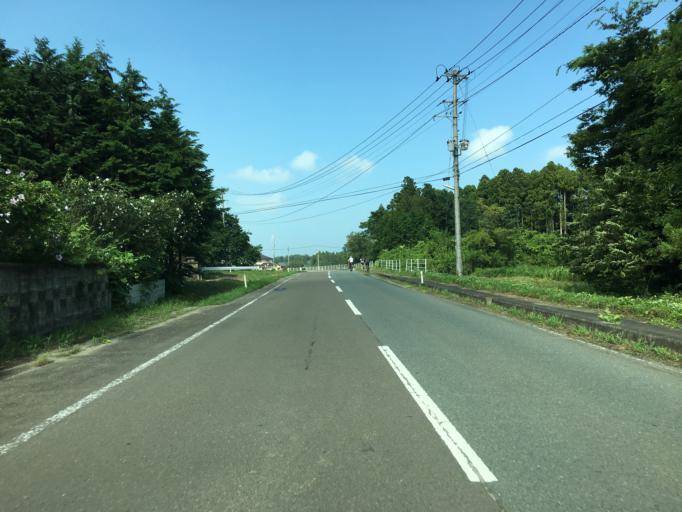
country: JP
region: Miyagi
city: Marumori
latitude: 37.8784
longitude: 140.8878
